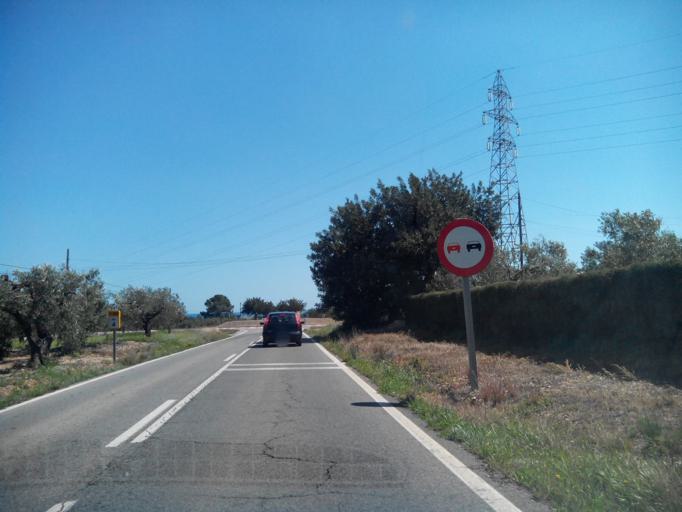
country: ES
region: Catalonia
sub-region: Provincia de Tarragona
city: Vilanova d'Escornalbou
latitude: 41.0769
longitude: 0.9690
